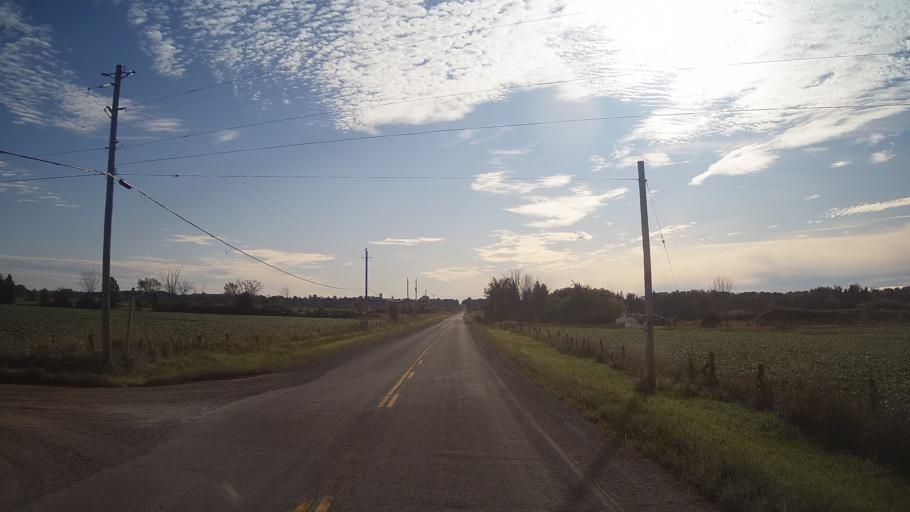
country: CA
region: Ontario
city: Gananoque
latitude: 44.4031
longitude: -76.0529
